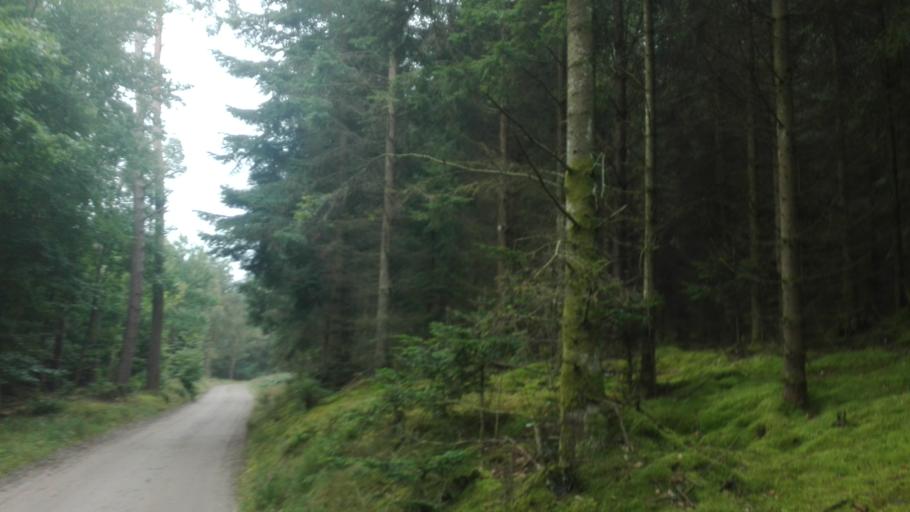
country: DK
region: Central Jutland
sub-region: Skanderborg Kommune
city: Ry
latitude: 56.0822
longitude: 9.7544
